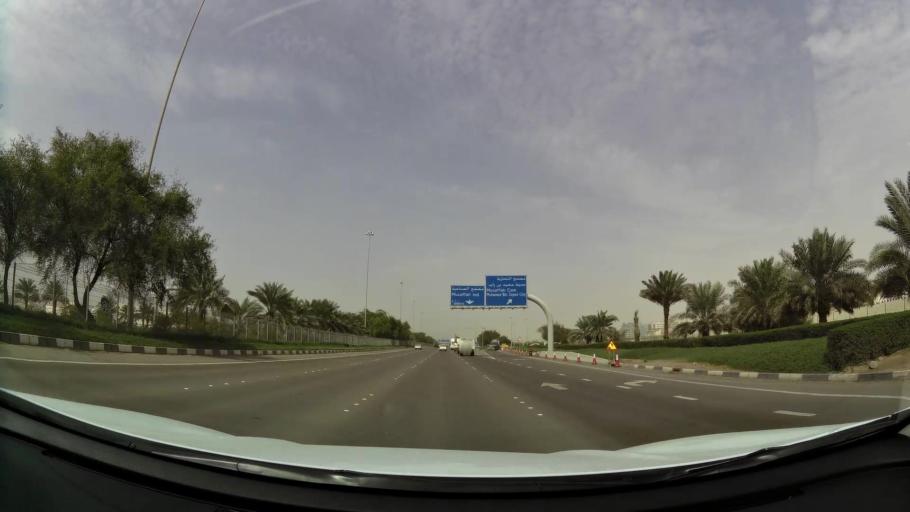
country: AE
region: Abu Dhabi
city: Abu Dhabi
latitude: 24.3364
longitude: 54.5268
